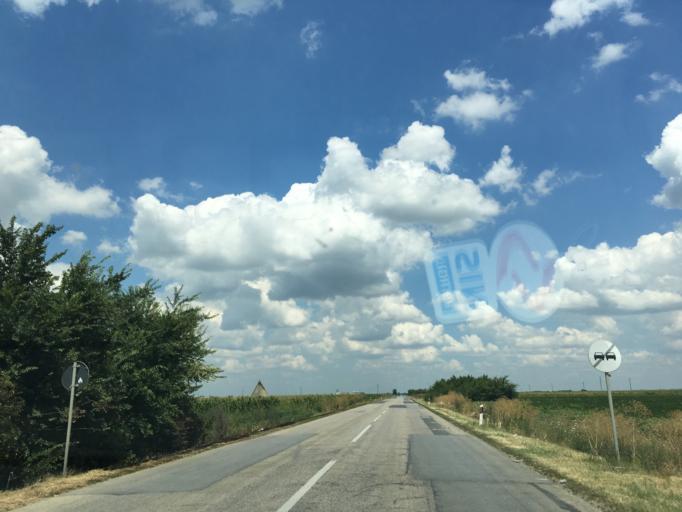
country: RS
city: Crepaja
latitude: 45.0390
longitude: 20.6388
